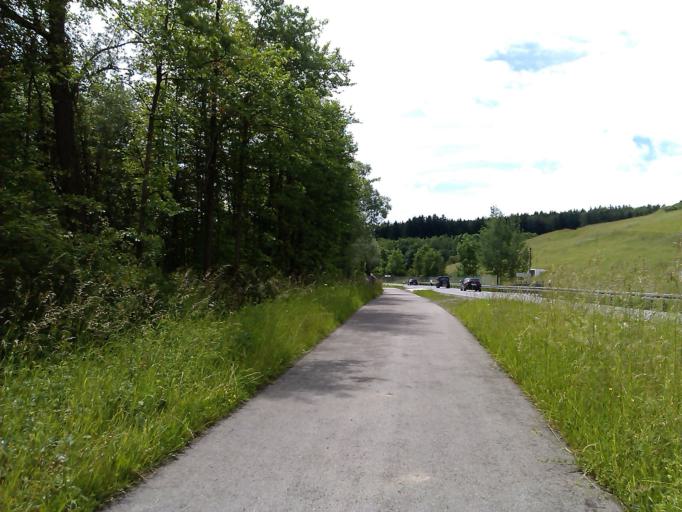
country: DE
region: Bavaria
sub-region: Swabia
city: Pforzen
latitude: 47.9063
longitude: 10.6084
